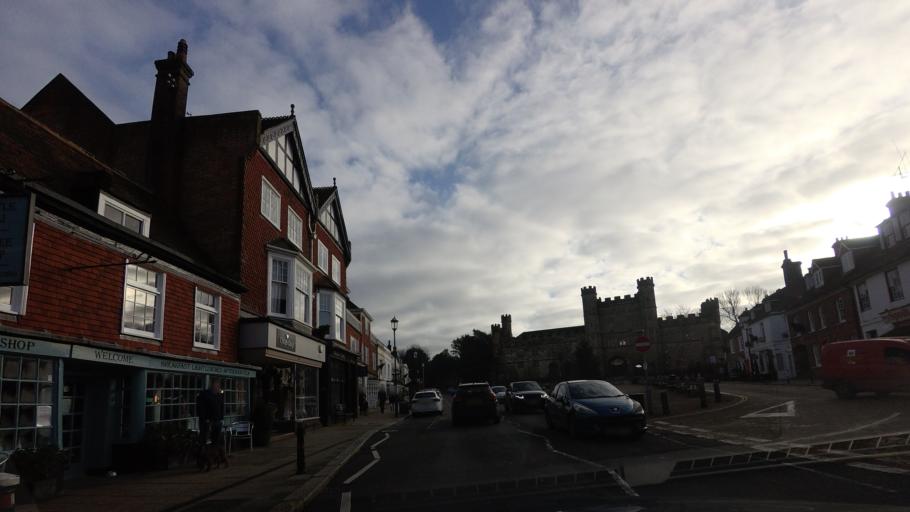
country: GB
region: England
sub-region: East Sussex
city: Battle
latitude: 50.9158
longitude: 0.4856
